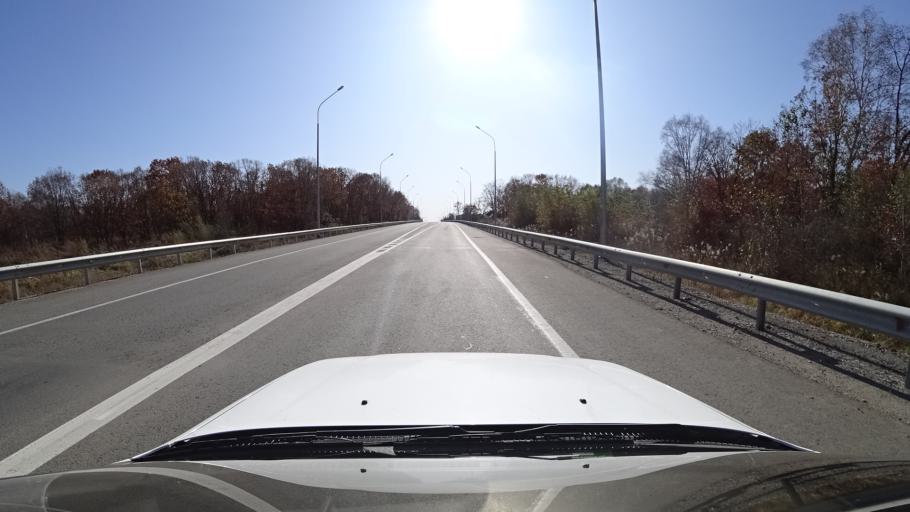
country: RU
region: Primorskiy
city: Dal'nerechensk
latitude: 45.8847
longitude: 133.7303
